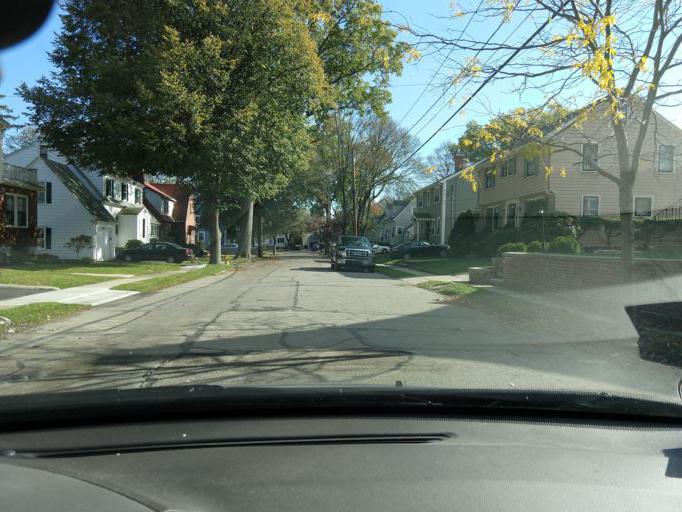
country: US
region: Massachusetts
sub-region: Middlesex County
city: Belmont
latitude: 42.3982
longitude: -71.1698
